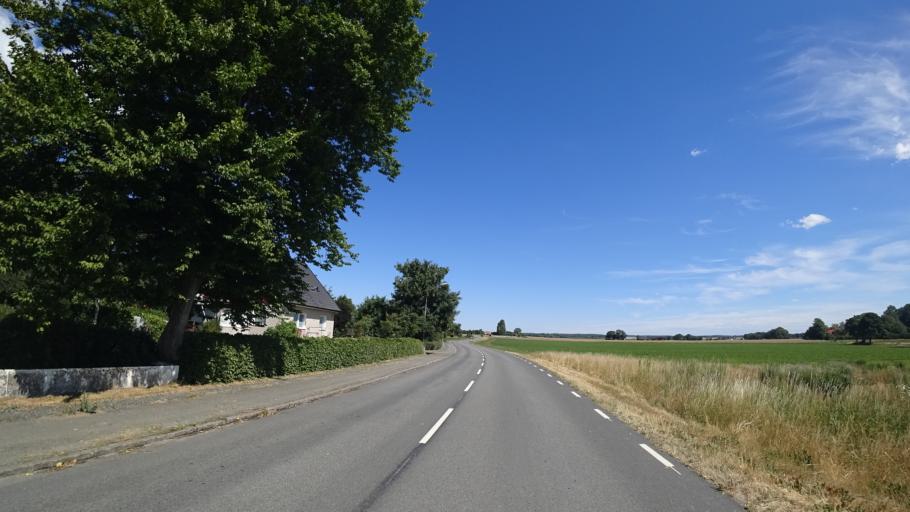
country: SE
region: Skane
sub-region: Kristianstads Kommun
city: Onnestad
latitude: 56.0646
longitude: 14.0268
